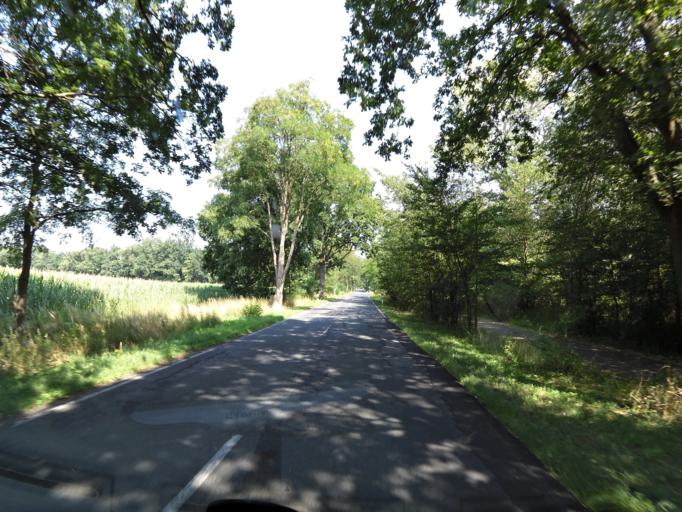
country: DE
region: Brandenburg
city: Liebenwalde
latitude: 52.8406
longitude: 13.3196
